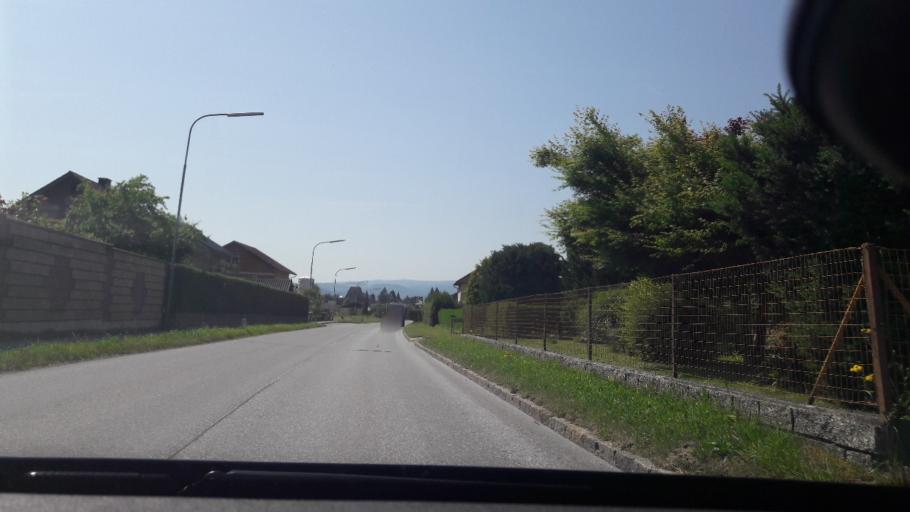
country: AT
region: Styria
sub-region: Politischer Bezirk Voitsberg
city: Kohlschwarz
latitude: 47.0889
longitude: 15.1225
